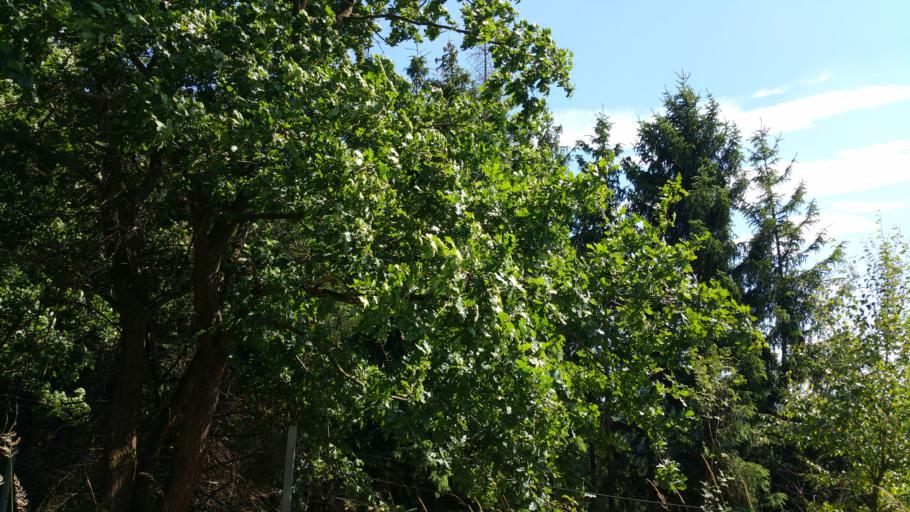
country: DE
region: Bavaria
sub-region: Upper Franconia
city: Topen
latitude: 50.3719
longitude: 11.8437
